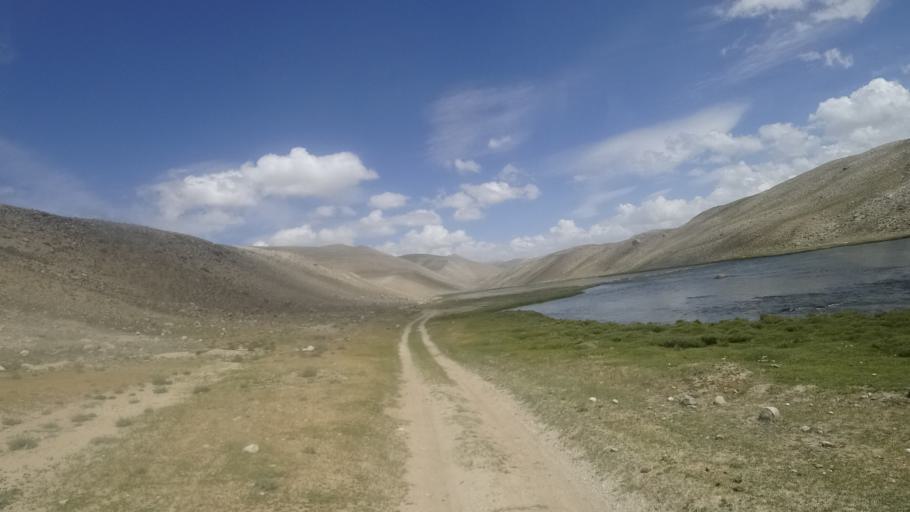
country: TJ
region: Gorno-Badakhshan
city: Murghob
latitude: 37.4724
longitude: 73.4425
